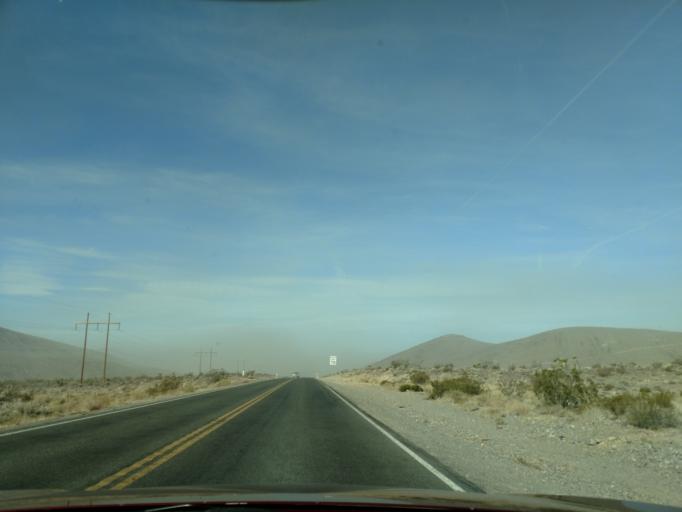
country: US
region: Nevada
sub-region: Nye County
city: Pahrump
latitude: 36.4371
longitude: -116.0793
